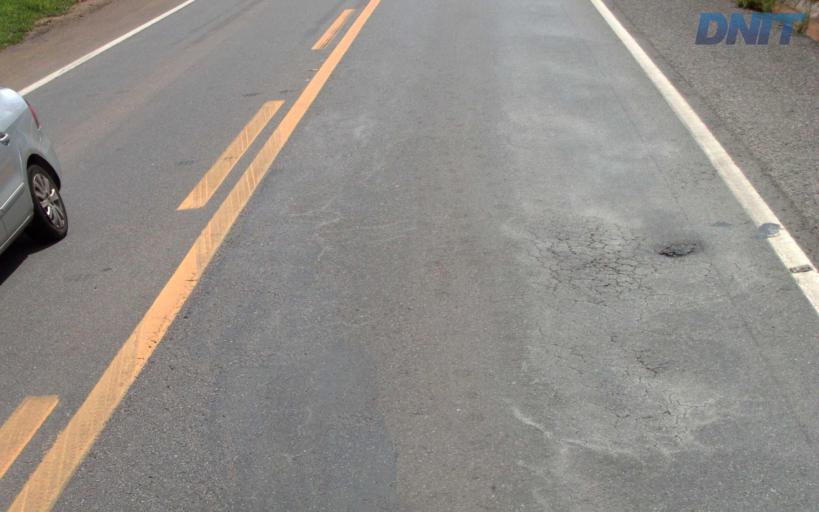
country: BR
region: Minas Gerais
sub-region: Belo Oriente
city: Belo Oriente
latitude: -19.1155
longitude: -42.2090
